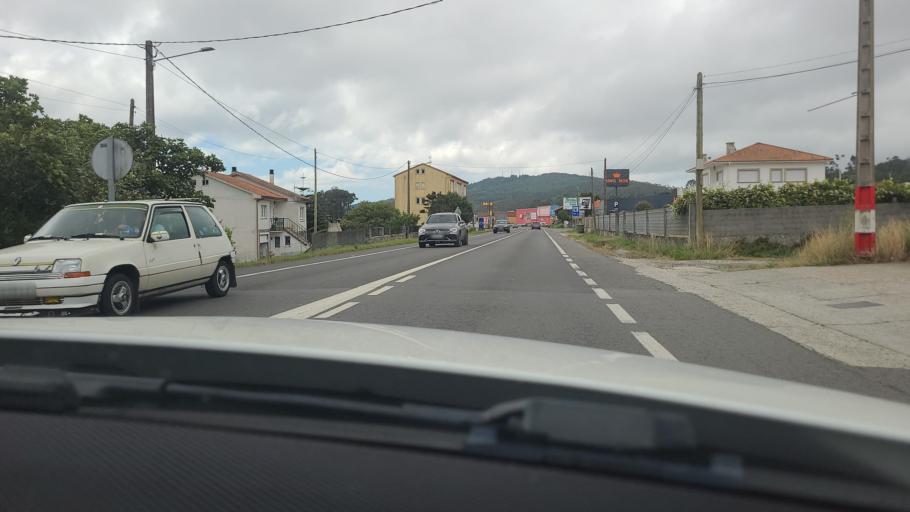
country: ES
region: Galicia
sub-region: Provincia da Coruna
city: Cee
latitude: 42.9716
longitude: -9.1908
